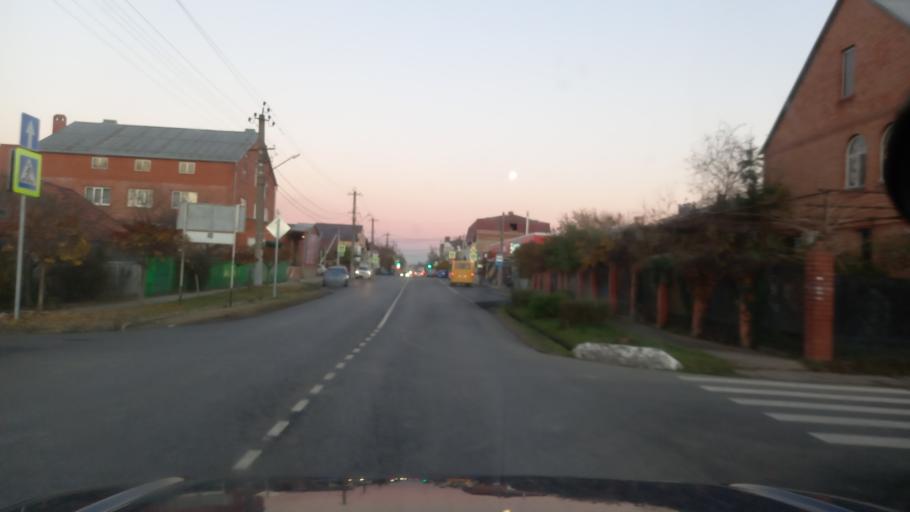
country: RU
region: Krasnodarskiy
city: Goryachiy Klyuch
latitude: 44.6284
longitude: 39.1045
